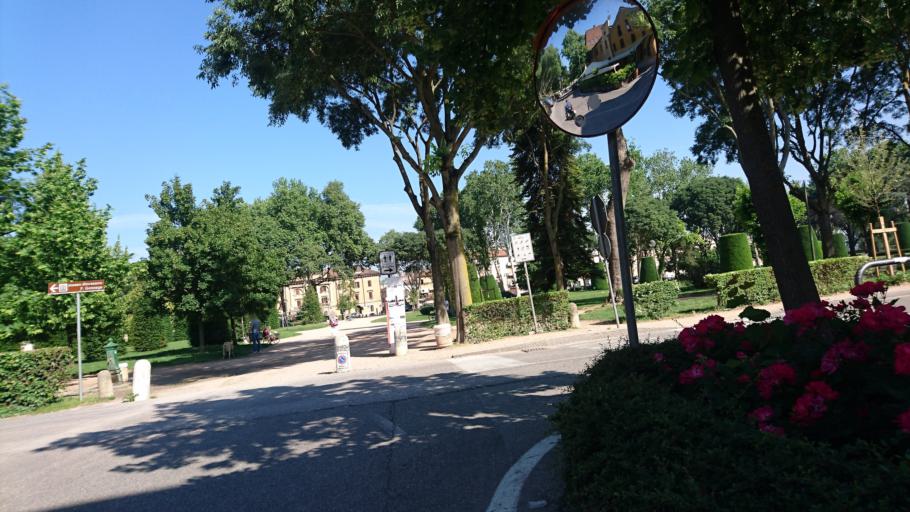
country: IT
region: Lombardy
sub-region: Provincia di Mantova
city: Mantova
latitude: 45.1620
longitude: 10.7952
